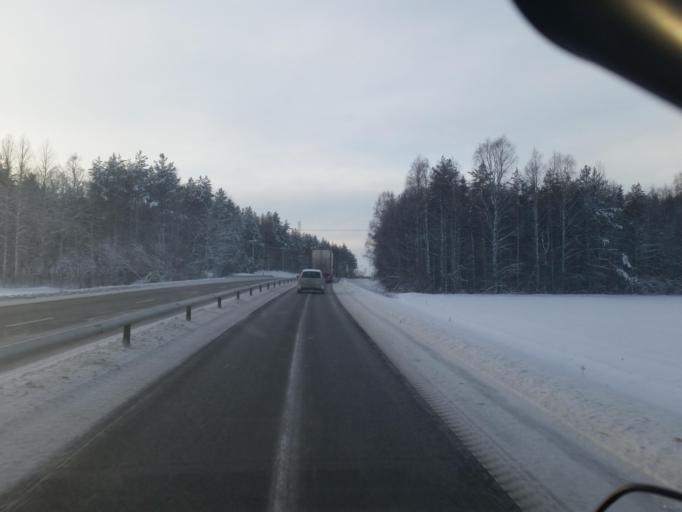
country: SE
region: Norrbotten
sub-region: Pitea Kommun
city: Norrfjarden
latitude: 65.4138
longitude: 21.5232
